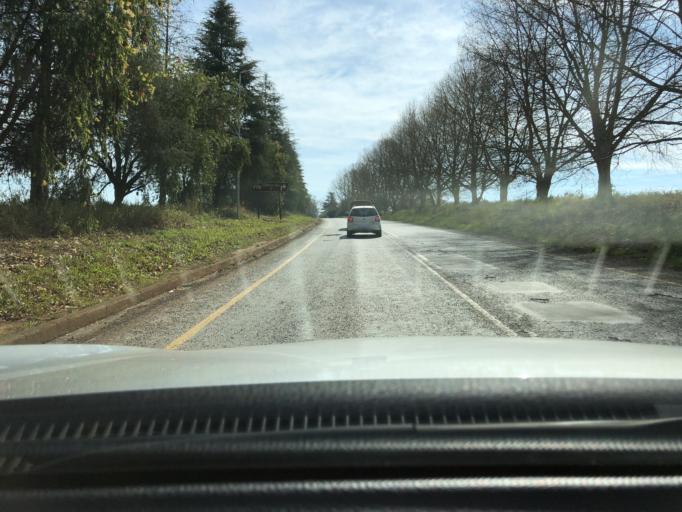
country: ZA
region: KwaZulu-Natal
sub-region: Sisonke District Municipality
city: Ixopo
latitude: -30.1368
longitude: 30.0803
